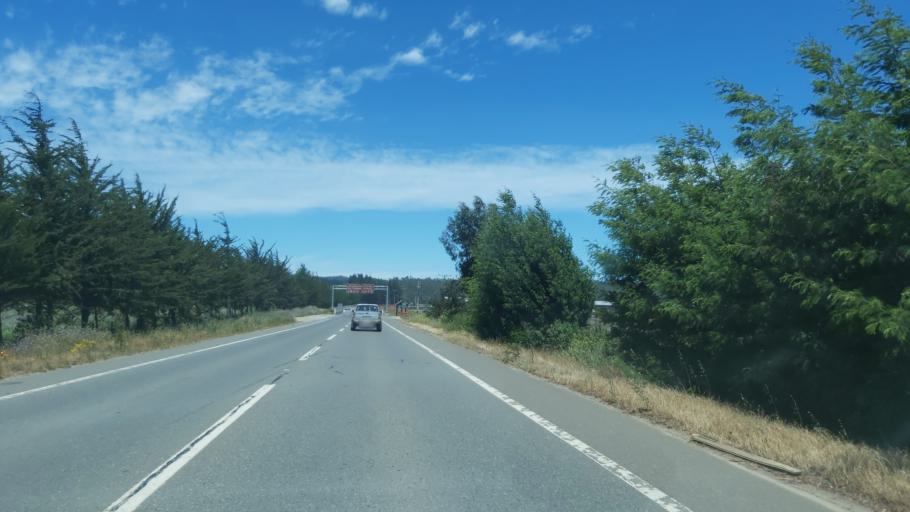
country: CL
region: Maule
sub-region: Provincia de Talca
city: Constitucion
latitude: -35.3073
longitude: -72.3794
